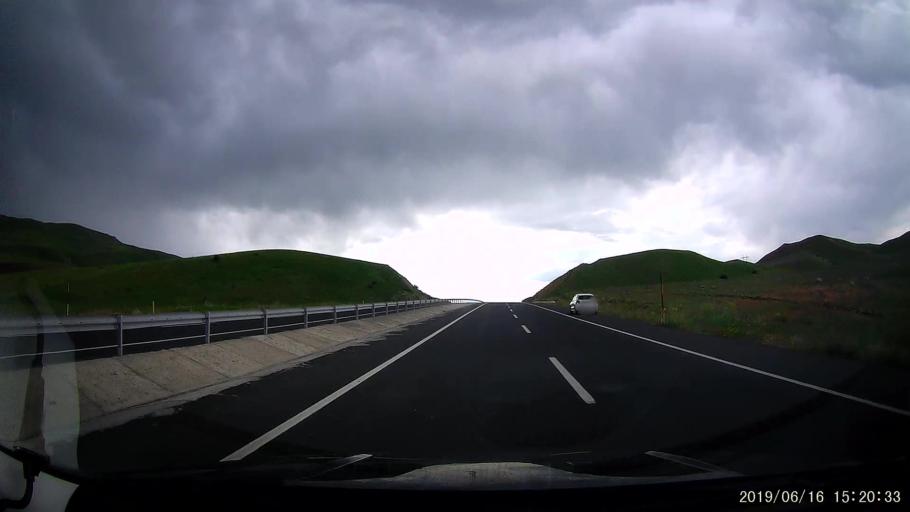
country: TR
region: Erzurum
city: Aras
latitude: 39.9743
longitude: 42.2633
